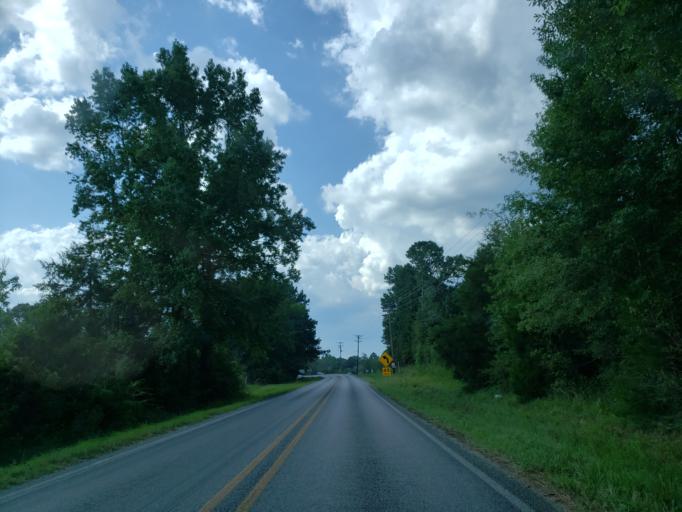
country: US
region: Mississippi
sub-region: Jones County
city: Sharon
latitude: 31.9172
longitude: -89.0194
